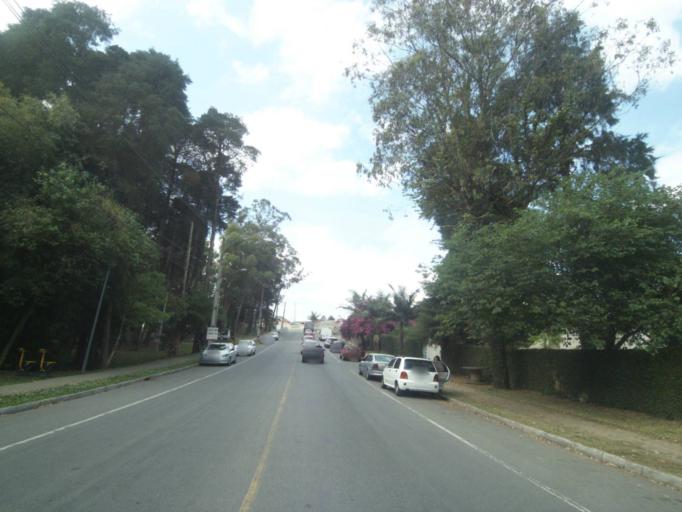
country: BR
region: Parana
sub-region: Pinhais
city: Pinhais
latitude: -25.4124
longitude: -49.2179
